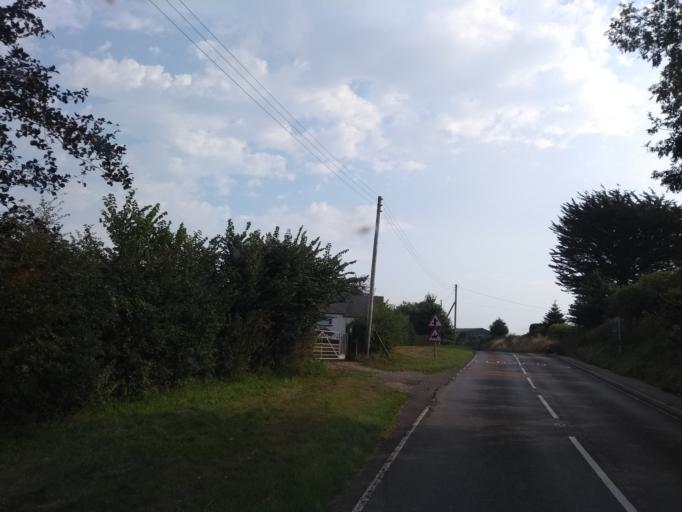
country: GB
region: England
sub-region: Devon
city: Colyton
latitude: 50.7500
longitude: -3.0289
